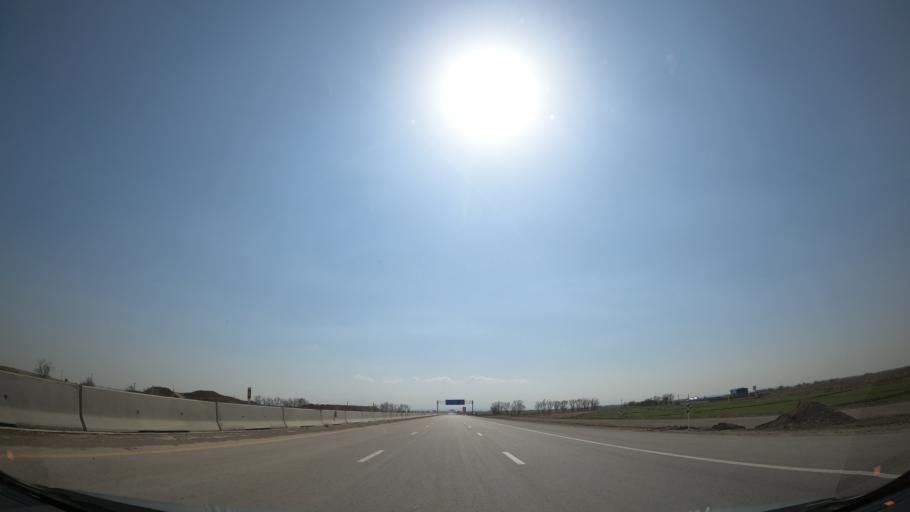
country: IR
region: Qazvin
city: Abyek
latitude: 35.9816
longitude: 50.4615
